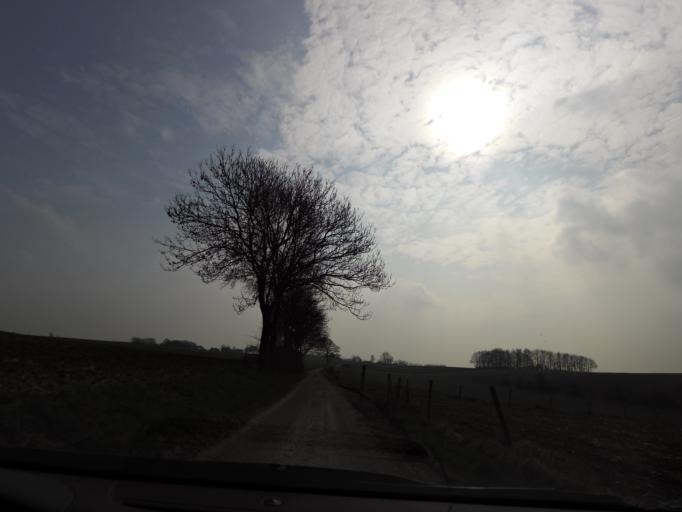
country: NL
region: Limburg
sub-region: Gemeente Voerendaal
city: Ubachsberg
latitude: 50.8440
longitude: 5.9286
